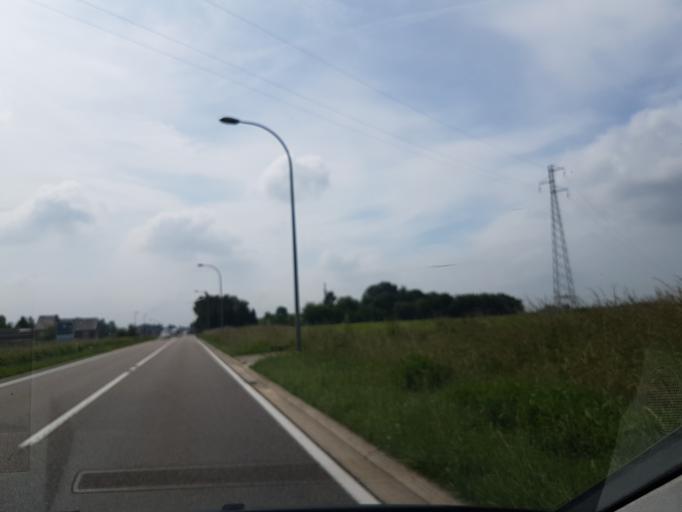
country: BE
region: Flanders
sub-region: Provincie Vlaams-Brabant
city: Asse
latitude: 50.9325
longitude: 4.1780
